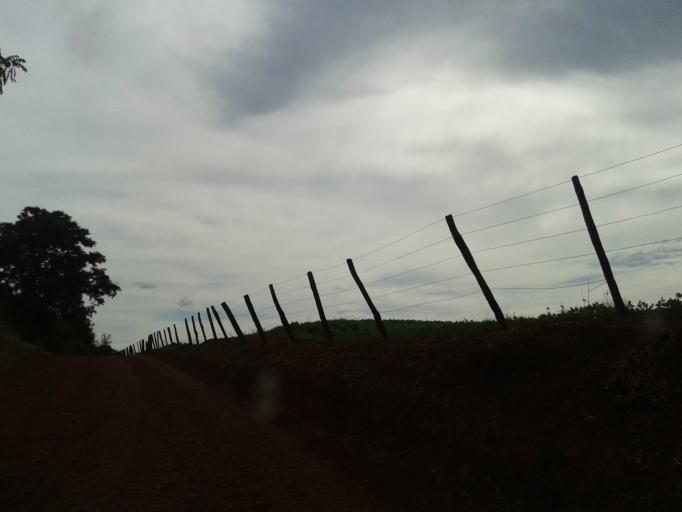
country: BR
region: Minas Gerais
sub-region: Centralina
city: Centralina
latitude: -18.6736
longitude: -49.3541
